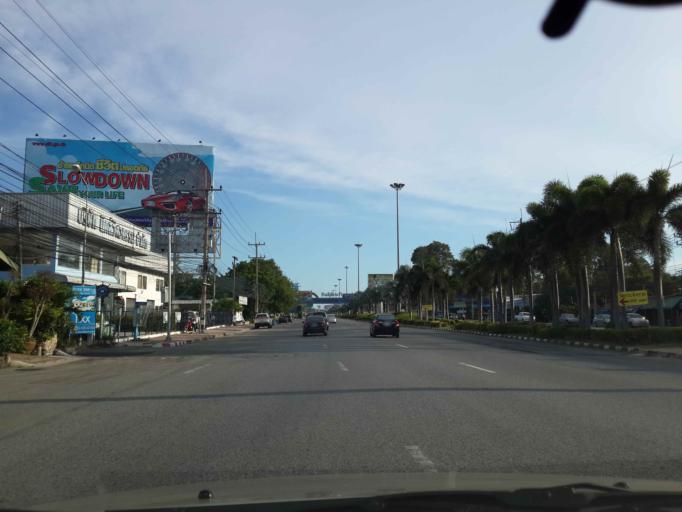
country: TH
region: Chon Buri
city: Bang Lamung
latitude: 12.9975
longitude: 100.9287
